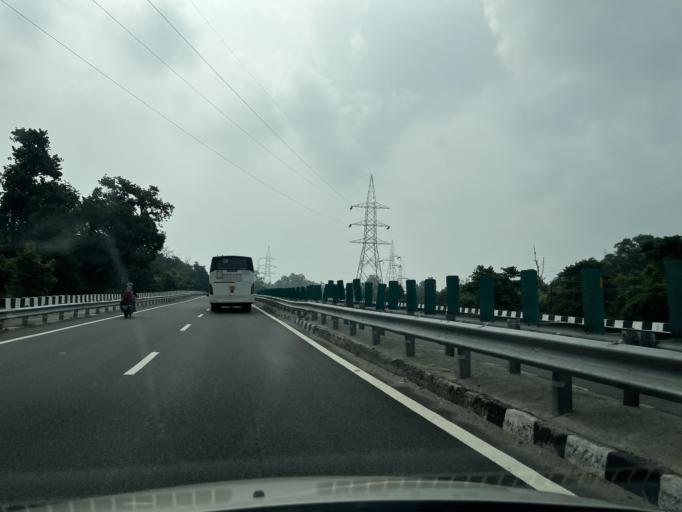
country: IN
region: Uttarakhand
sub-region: Dehradun
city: Raiwala
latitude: 30.0709
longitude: 78.2046
